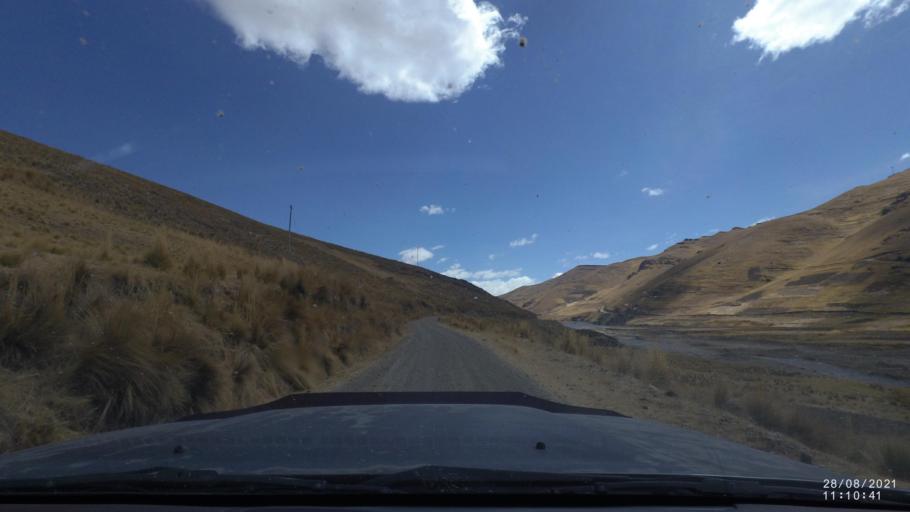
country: BO
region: Cochabamba
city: Cochabamba
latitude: -17.1555
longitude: -66.3123
